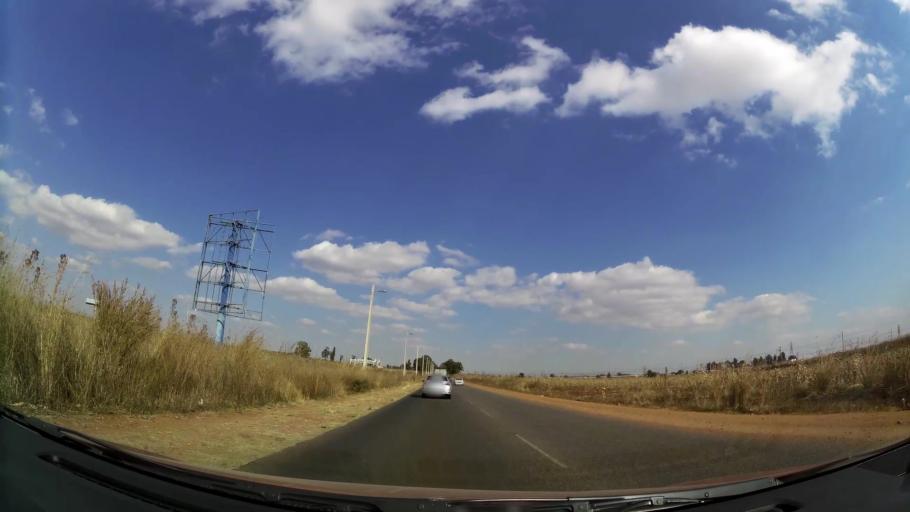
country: ZA
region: Gauteng
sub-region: Ekurhuleni Metropolitan Municipality
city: Tembisa
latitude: -25.9929
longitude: 28.2493
